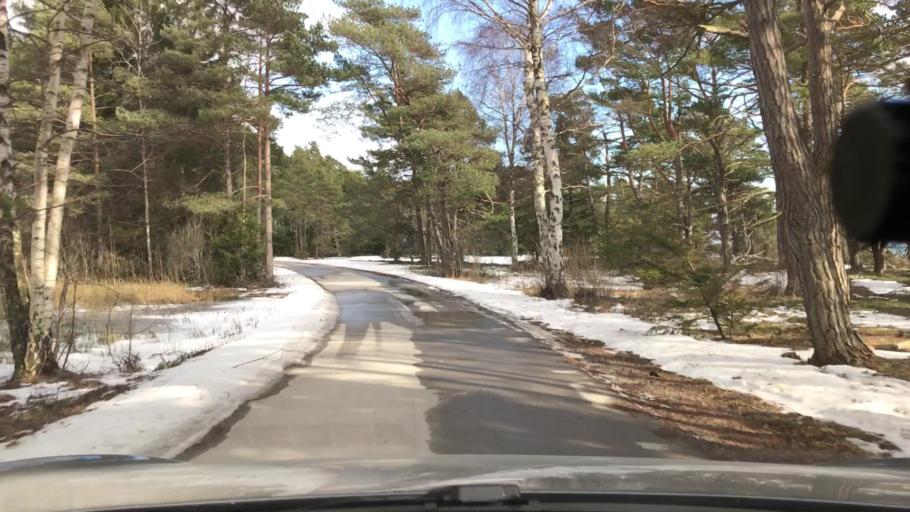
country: SE
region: Gotland
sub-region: Gotland
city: Hemse
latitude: 57.3434
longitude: 18.7261
